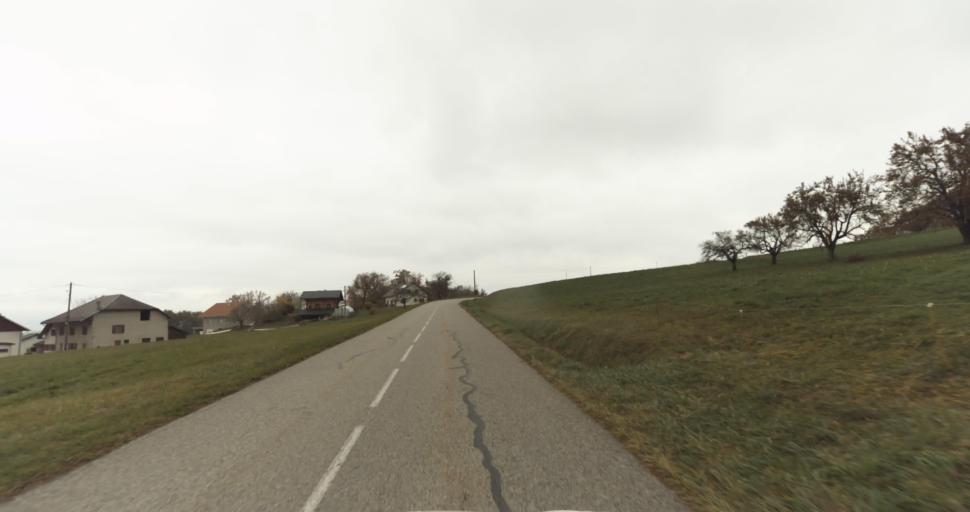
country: FR
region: Rhone-Alpes
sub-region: Departement de la Haute-Savoie
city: Saint-Felix
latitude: 45.7991
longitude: 5.9930
